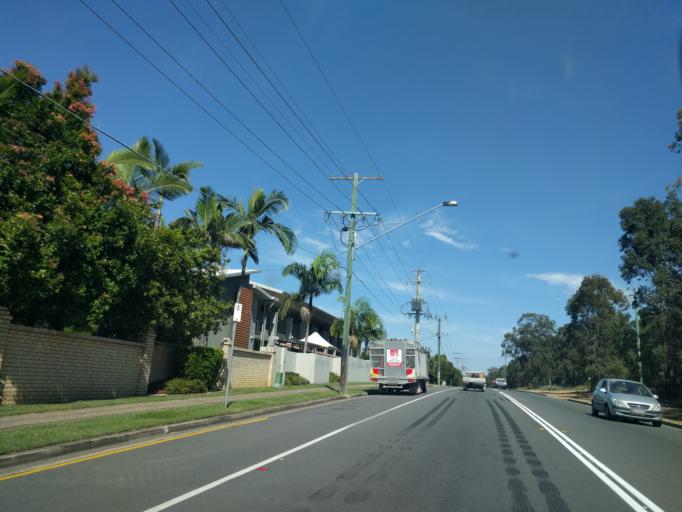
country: AU
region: Queensland
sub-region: Brisbane
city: Sunnybank Hills
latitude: -27.6588
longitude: 153.0282
